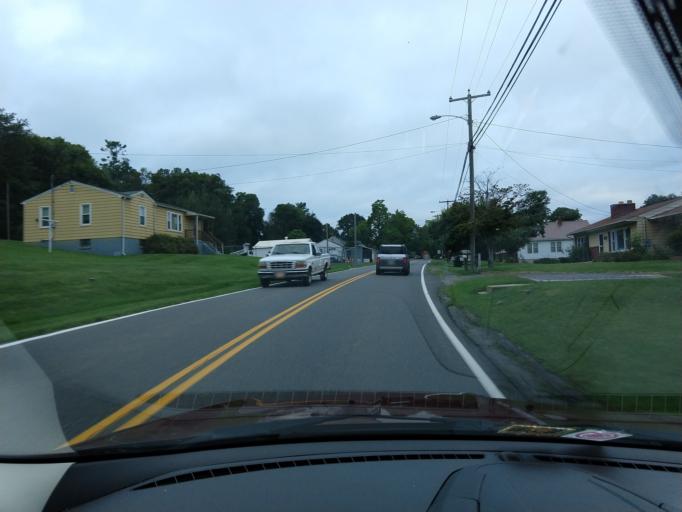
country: US
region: Virginia
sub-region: City of Covington
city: Fairlawn
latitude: 37.7527
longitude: -79.9902
